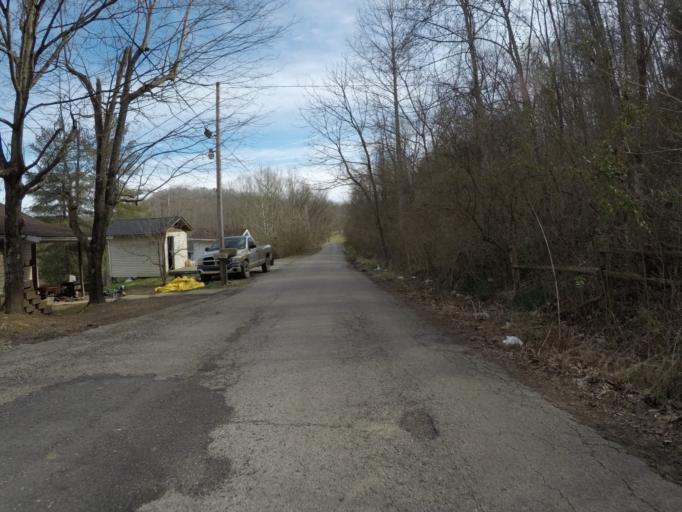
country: US
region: West Virginia
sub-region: Wayne County
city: Lavalette
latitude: 38.3398
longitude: -82.5045
